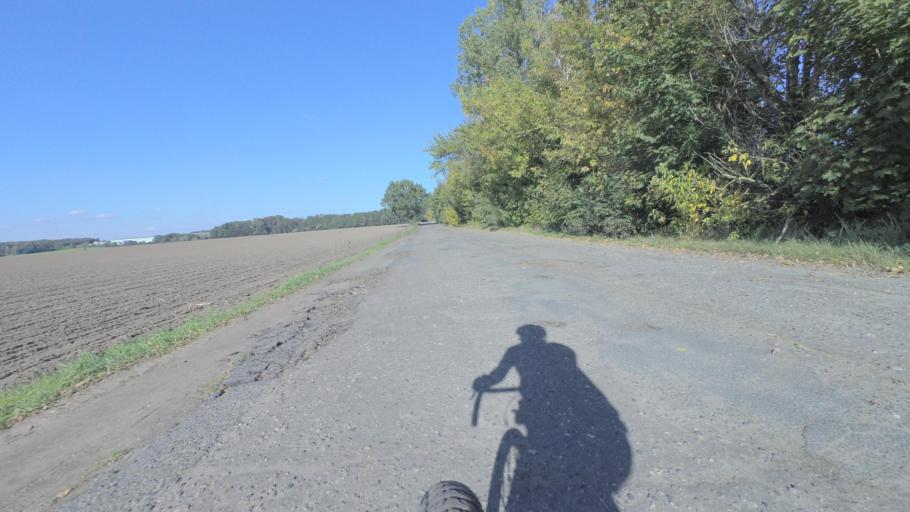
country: DE
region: Brandenburg
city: Rangsdorf
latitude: 52.2820
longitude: 13.4684
